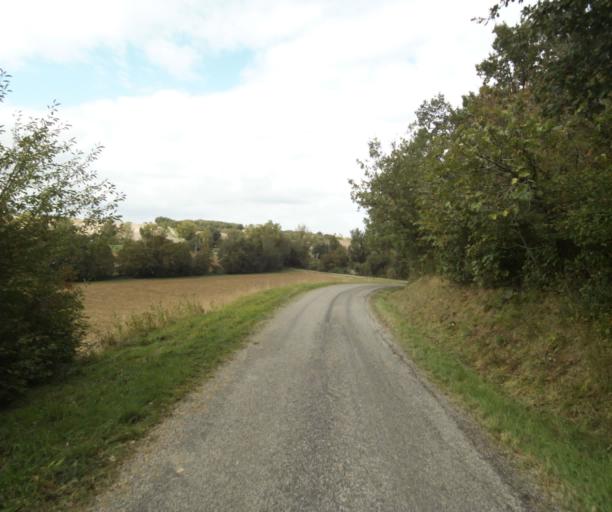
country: FR
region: Midi-Pyrenees
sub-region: Departement du Tarn-et-Garonne
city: Beaumont-de-Lomagne
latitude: 43.8902
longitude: 1.0805
